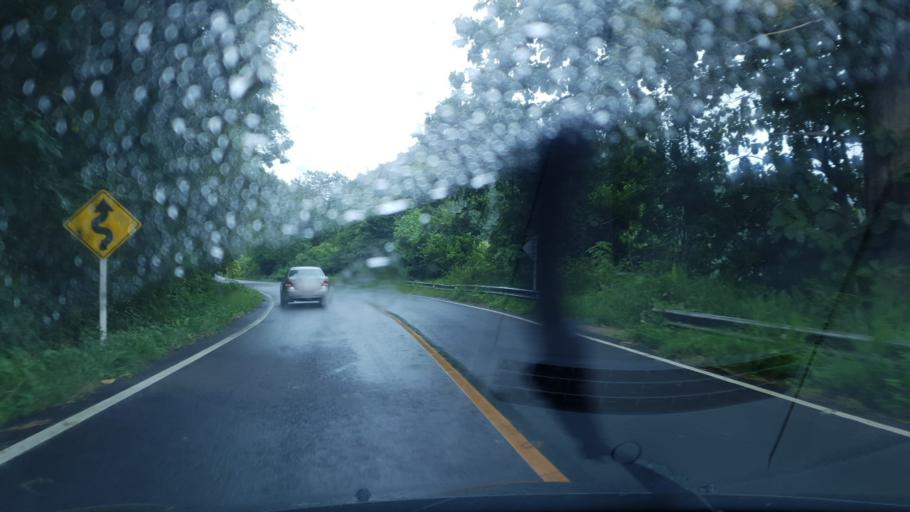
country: TH
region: Mae Hong Son
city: Khun Yuam
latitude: 18.6770
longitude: 97.9232
